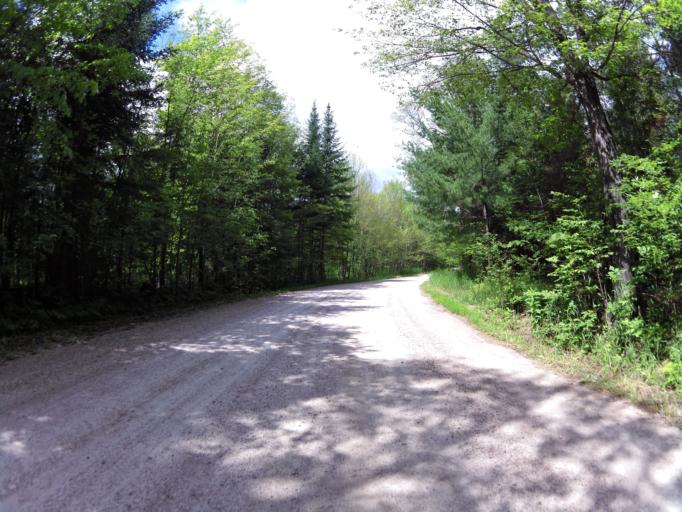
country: CA
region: Ontario
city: Perth
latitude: 45.0259
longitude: -76.5132
